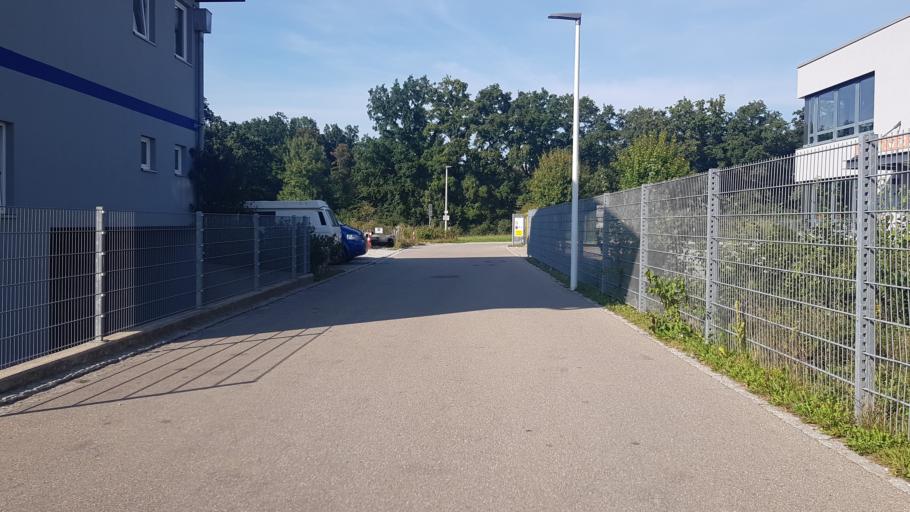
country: DE
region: Bavaria
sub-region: Upper Bavaria
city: Wessling
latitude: 48.0809
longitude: 11.2683
